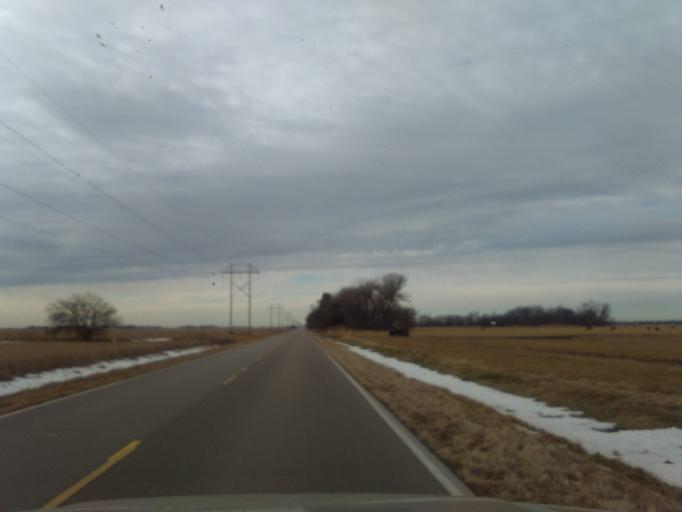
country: US
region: Nebraska
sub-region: Buffalo County
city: Gibbon
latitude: 40.6550
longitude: -98.8088
